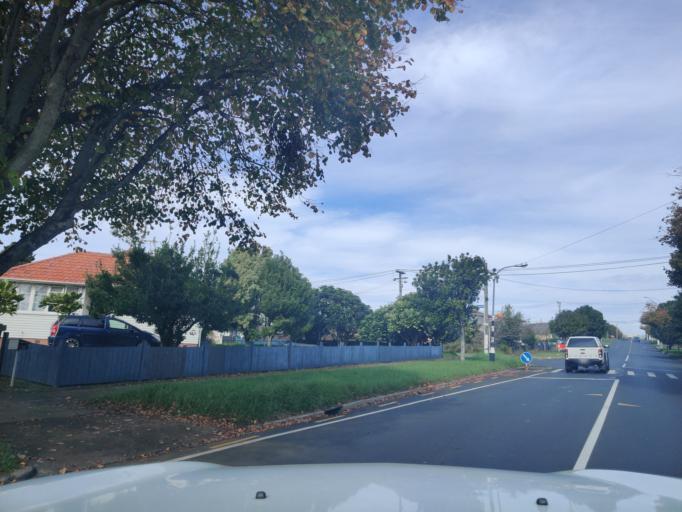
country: NZ
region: Auckland
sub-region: Auckland
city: Tamaki
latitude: -36.8981
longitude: 174.8599
